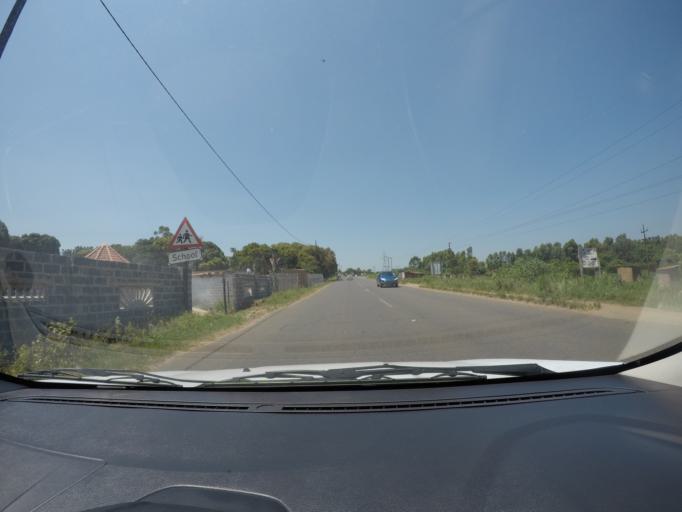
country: ZA
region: KwaZulu-Natal
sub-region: uThungulu District Municipality
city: eSikhawini
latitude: -28.8289
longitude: 31.9426
